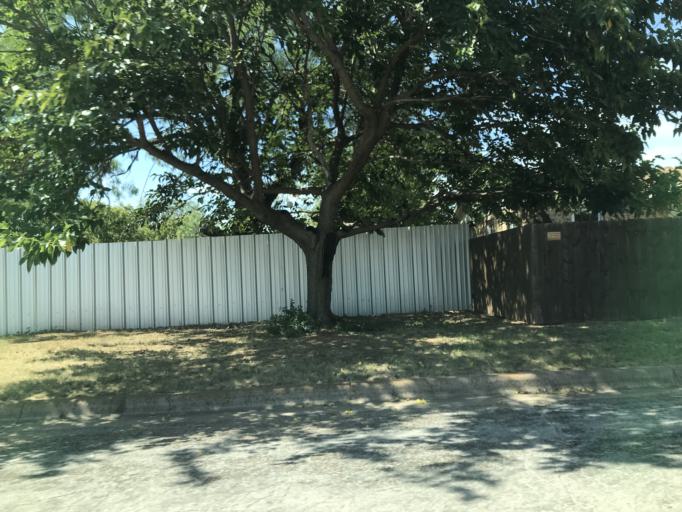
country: US
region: Texas
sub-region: Taylor County
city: Abilene
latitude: 32.4239
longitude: -99.7502
